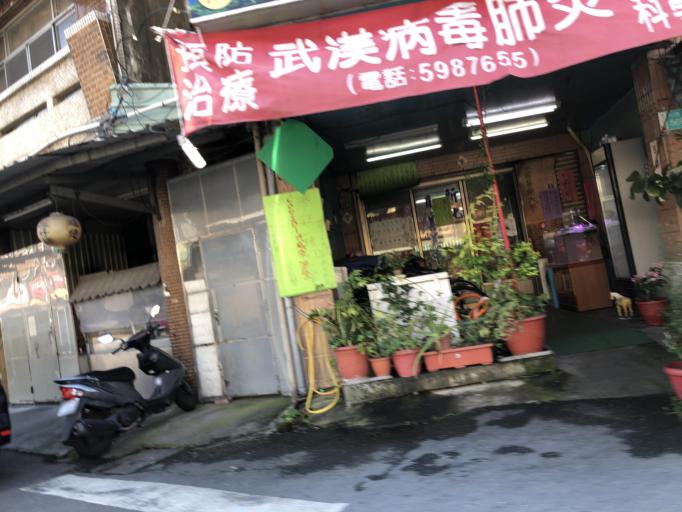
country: TW
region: Taiwan
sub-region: Tainan
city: Tainan
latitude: 23.0361
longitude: 120.3013
